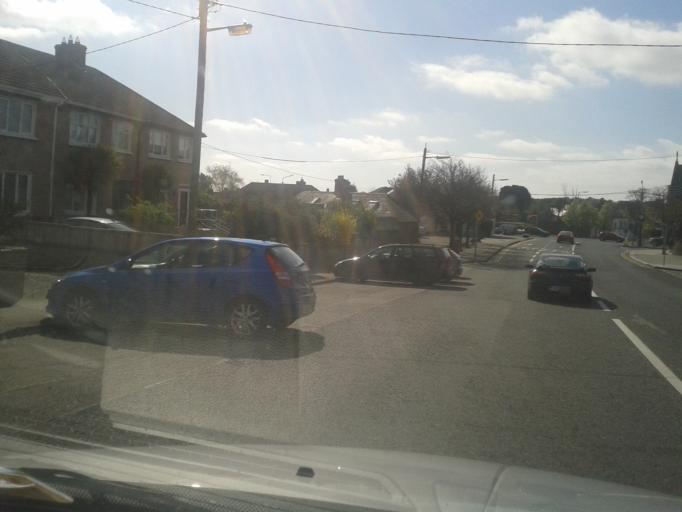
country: IE
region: Leinster
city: Raheny
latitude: 53.3813
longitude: -6.1758
